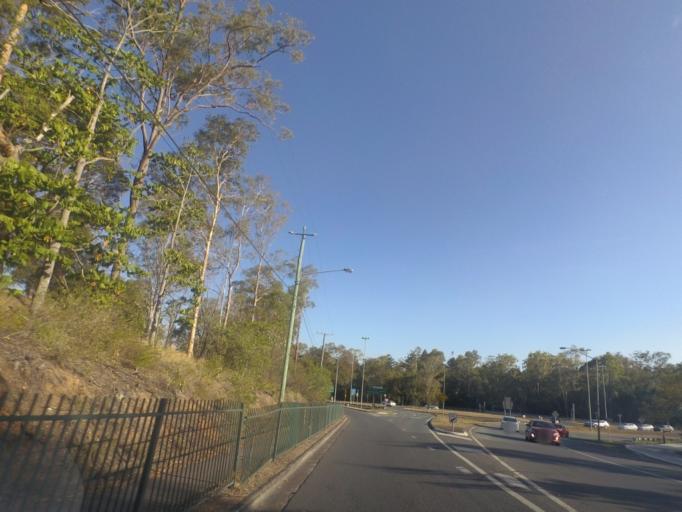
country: AU
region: Queensland
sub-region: Brisbane
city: Toowong
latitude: -27.4767
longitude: 152.9807
